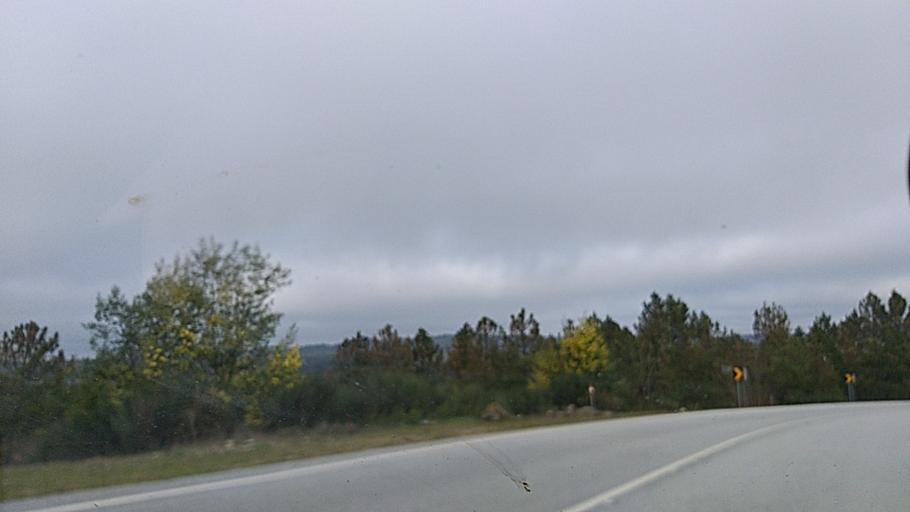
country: PT
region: Guarda
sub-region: Fornos de Algodres
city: Fornos de Algodres
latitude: 40.7107
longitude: -7.4862
